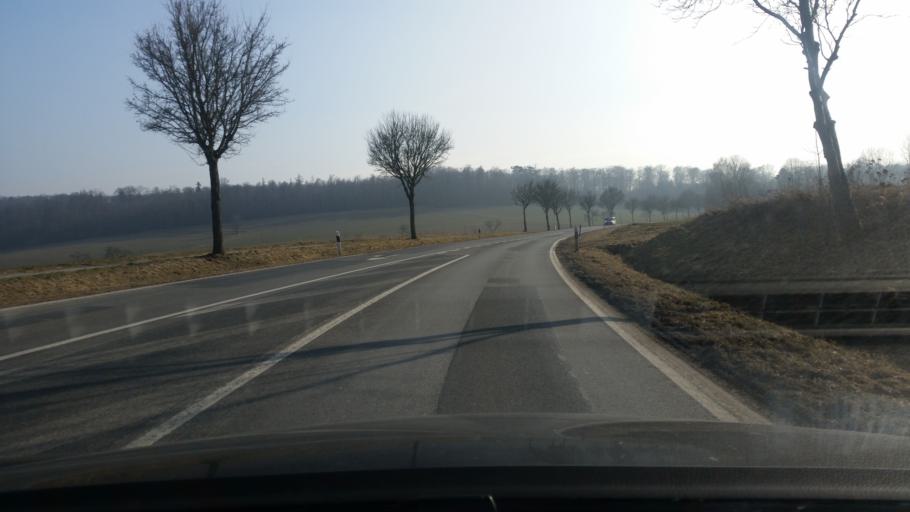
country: DE
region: Lower Saxony
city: Hameln
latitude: 52.1313
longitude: 9.3804
